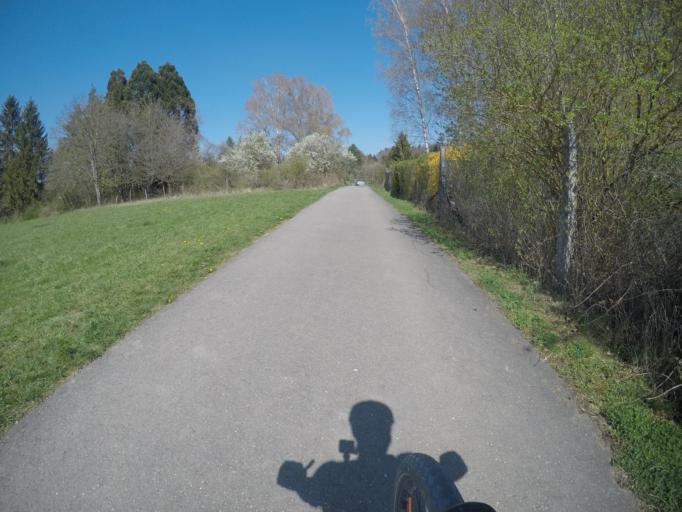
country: DE
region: Baden-Wuerttemberg
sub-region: Regierungsbezirk Stuttgart
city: Magstadt
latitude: 48.7521
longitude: 8.9681
